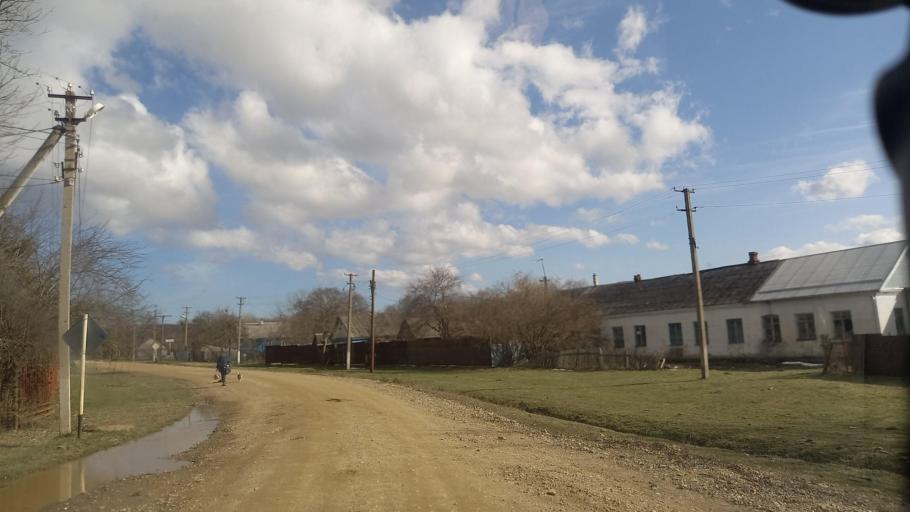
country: RU
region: Krasnodarskiy
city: Smolenskaya
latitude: 44.6027
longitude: 38.8588
